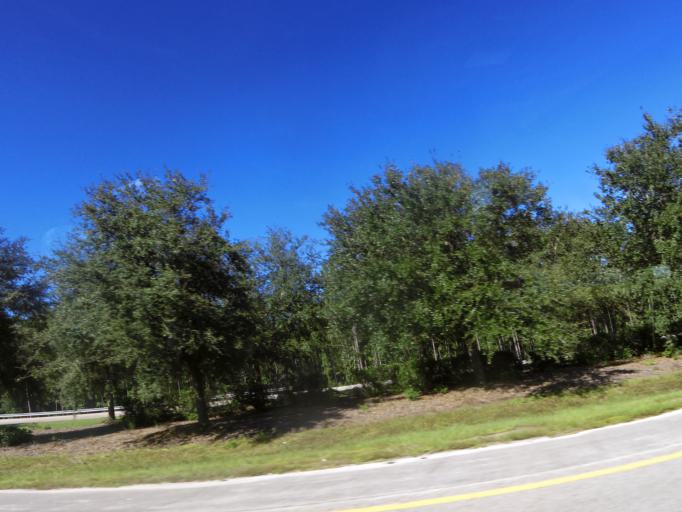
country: US
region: Florida
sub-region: Saint Johns County
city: Palm Valley
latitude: 30.1147
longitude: -81.4298
